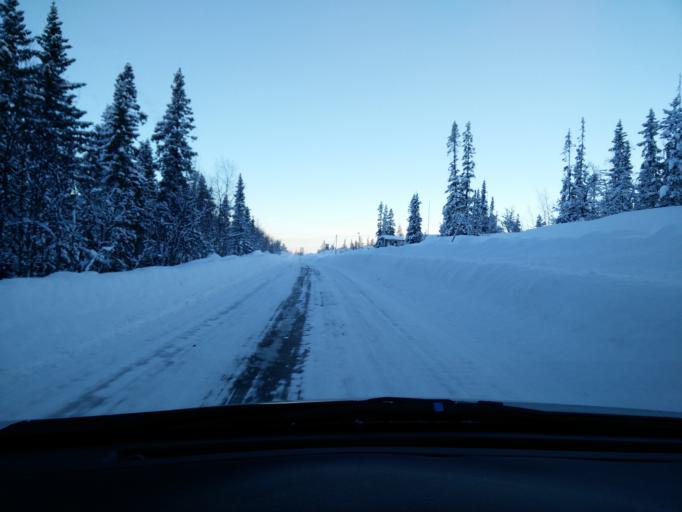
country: SE
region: Jaemtland
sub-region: Bergs Kommun
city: Hoverberg
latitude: 62.4967
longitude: 14.1119
